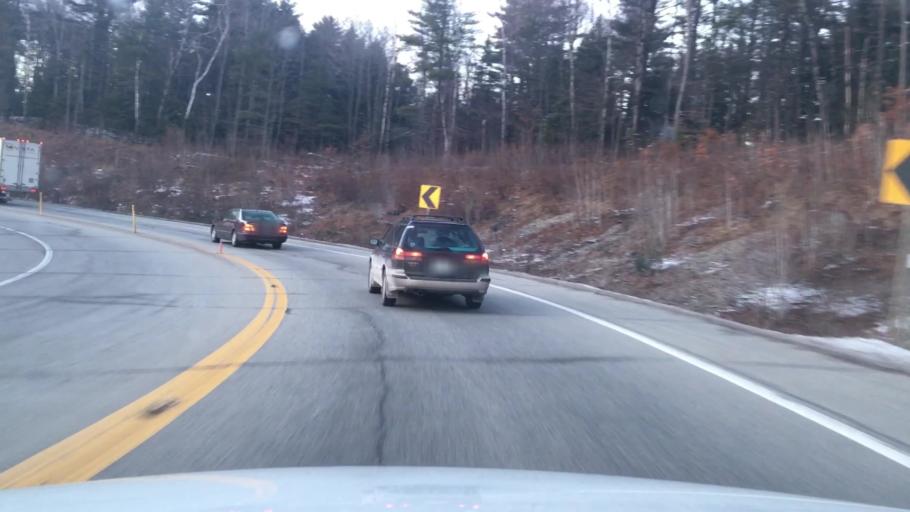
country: US
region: Maine
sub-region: Androscoggin County
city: Minot
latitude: 44.0388
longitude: -70.2689
